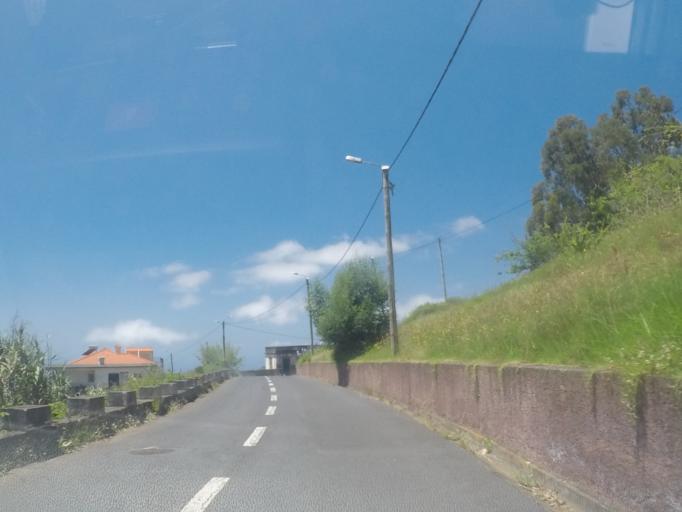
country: PT
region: Madeira
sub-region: Camara de Lobos
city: Curral das Freiras
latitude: 32.6870
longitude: -16.9826
